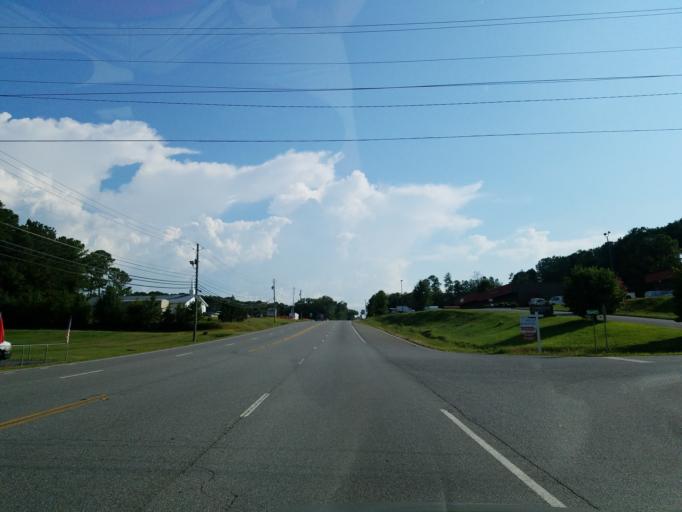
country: US
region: Georgia
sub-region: Bartow County
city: Cartersville
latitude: 34.2177
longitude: -84.7922
